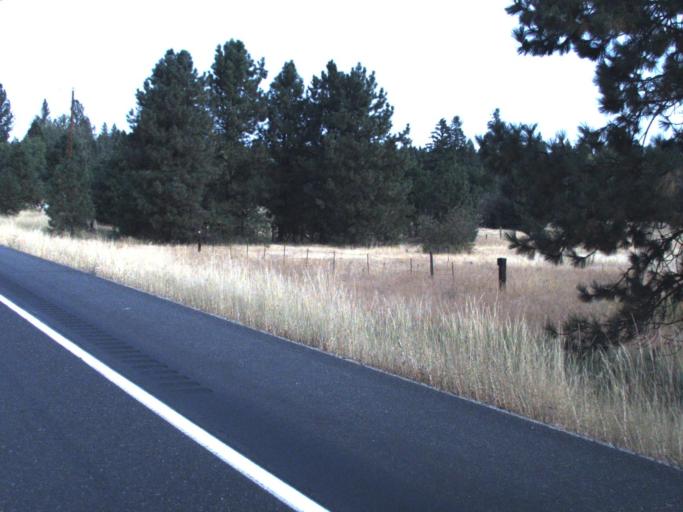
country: US
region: Washington
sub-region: Spokane County
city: Deer Park
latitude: 47.8812
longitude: -117.4224
